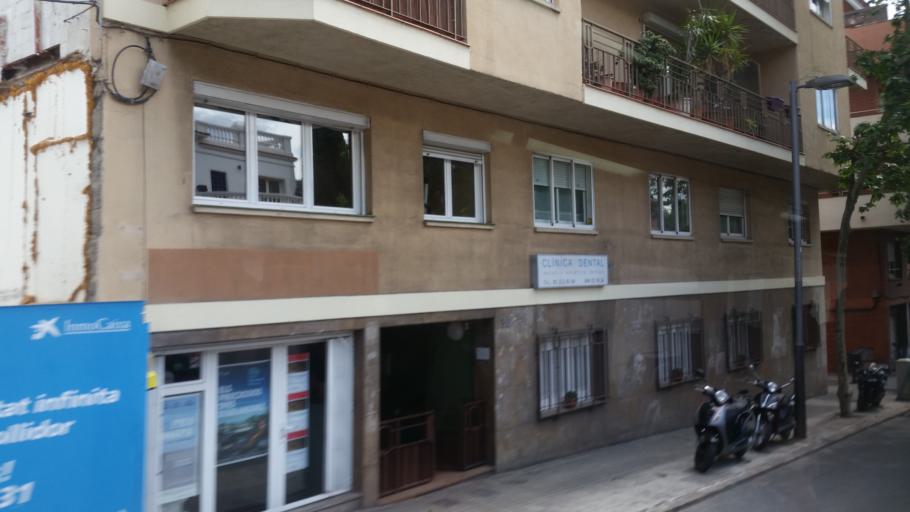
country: ES
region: Catalonia
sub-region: Provincia de Barcelona
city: Sarria-Sant Gervasi
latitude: 41.4153
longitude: 2.1463
